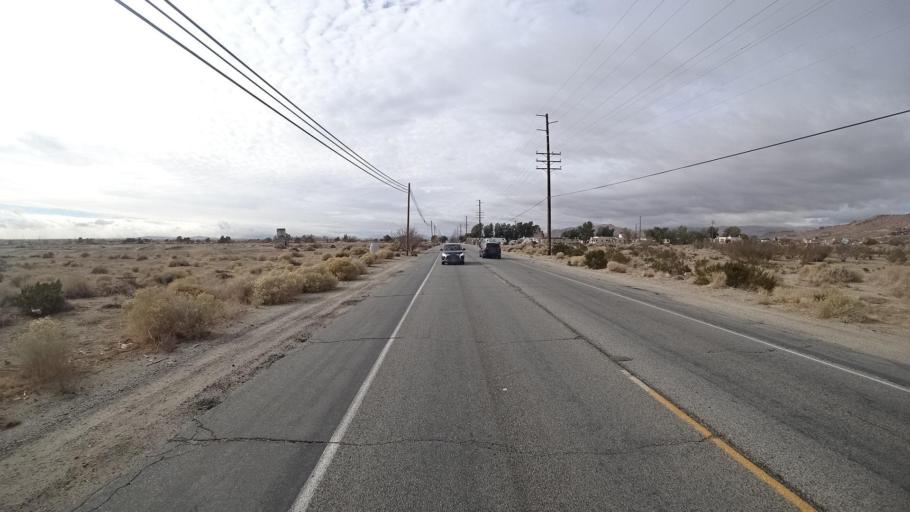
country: US
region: California
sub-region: Kern County
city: Rosamond
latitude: 34.8637
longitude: -118.2231
